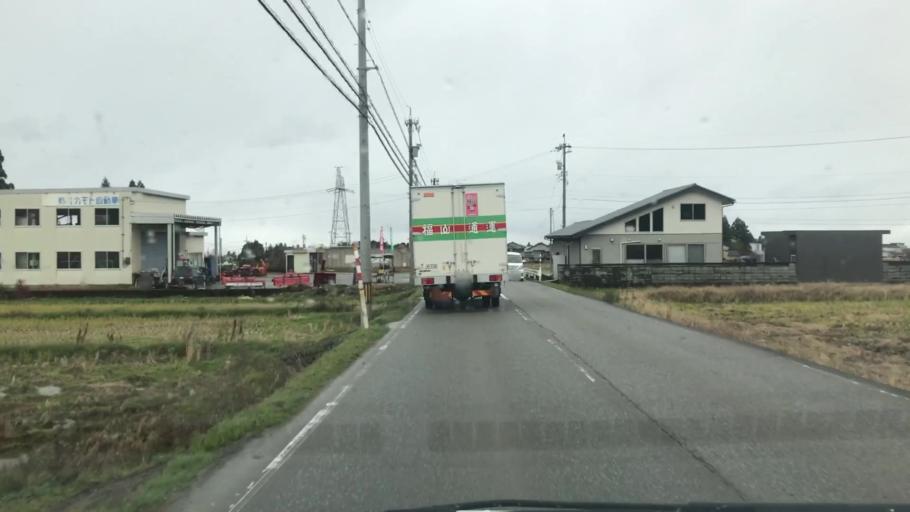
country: JP
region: Toyama
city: Kamiichi
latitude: 36.5975
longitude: 137.3245
